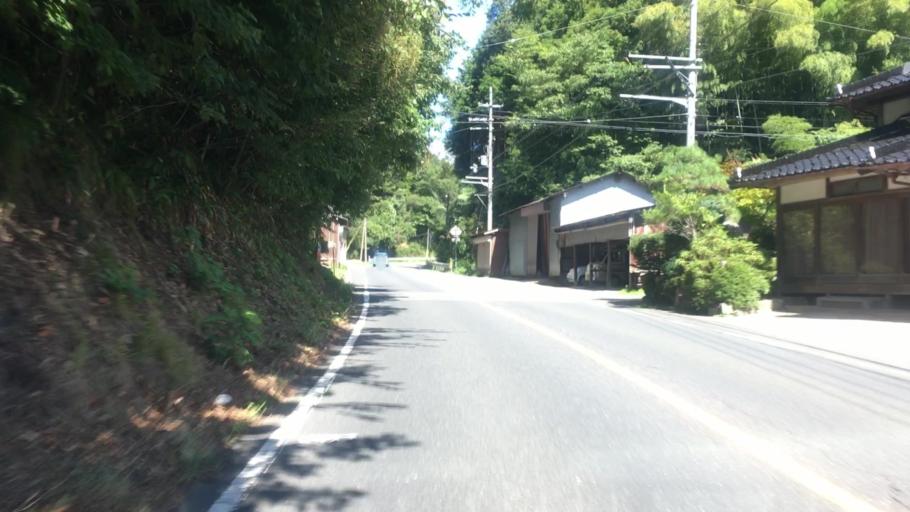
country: JP
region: Hyogo
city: Toyooka
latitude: 35.5941
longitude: 134.9071
